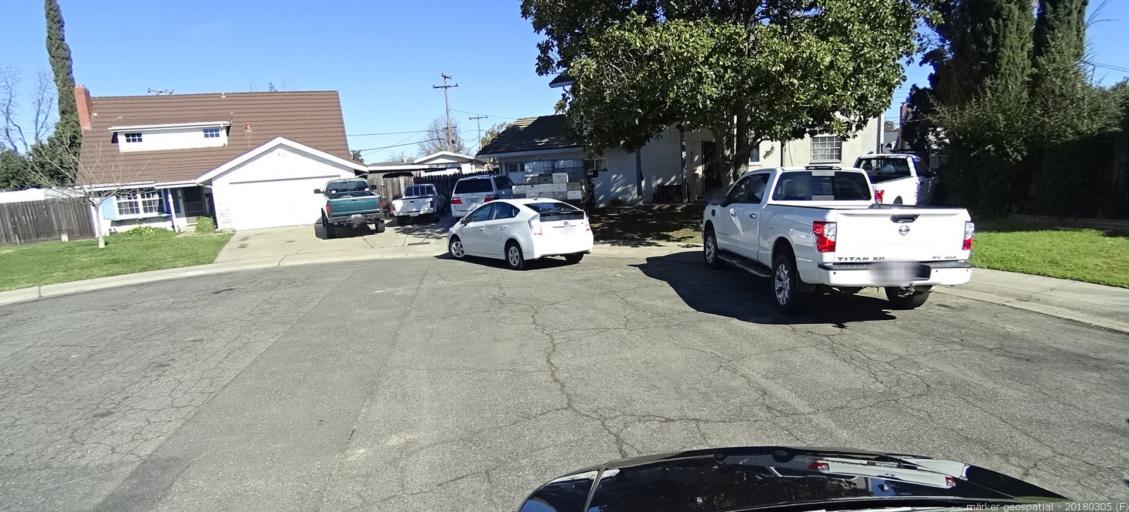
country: US
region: California
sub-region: Sacramento County
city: Florin
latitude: 38.4933
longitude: -121.4217
